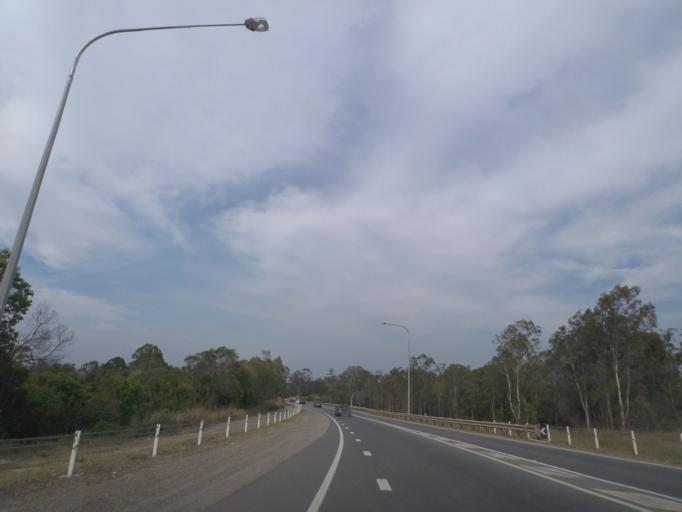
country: AU
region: Queensland
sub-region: Brisbane
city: Sunnybank
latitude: -27.5979
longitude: 153.0139
